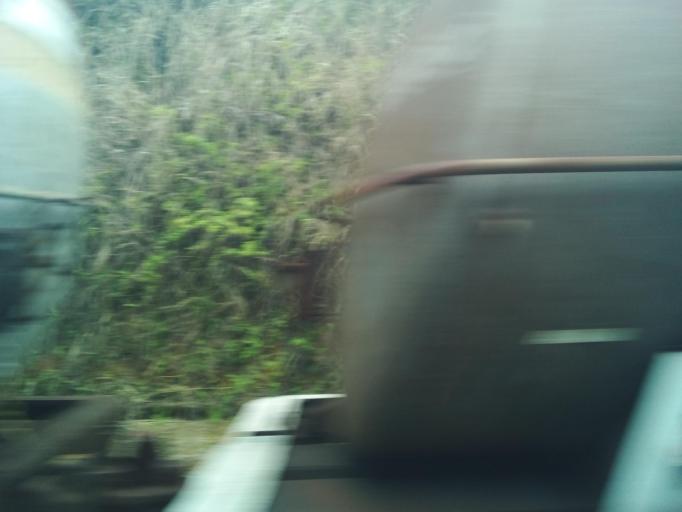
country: BR
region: Minas Gerais
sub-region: Coronel Fabriciano
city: Coronel Fabriciano
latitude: -19.5175
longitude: -42.5755
